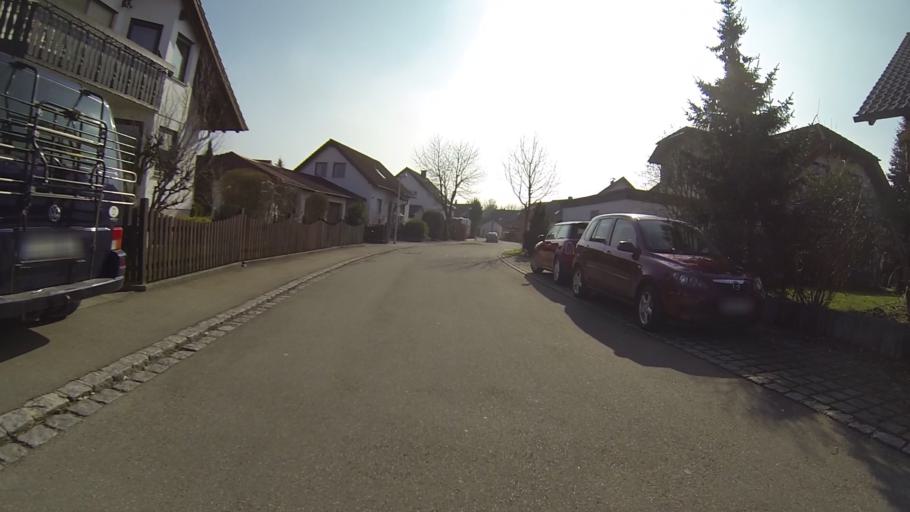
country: DE
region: Baden-Wuerttemberg
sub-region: Regierungsbezirk Stuttgart
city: Bolheim
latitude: 48.6338
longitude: 10.1560
